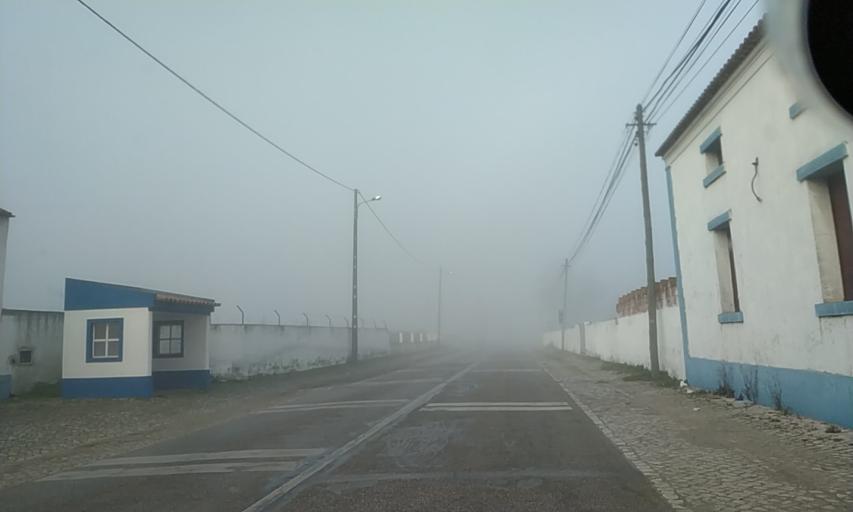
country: PT
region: Setubal
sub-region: Palmela
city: Pinhal Novo
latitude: 38.6127
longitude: -8.8787
